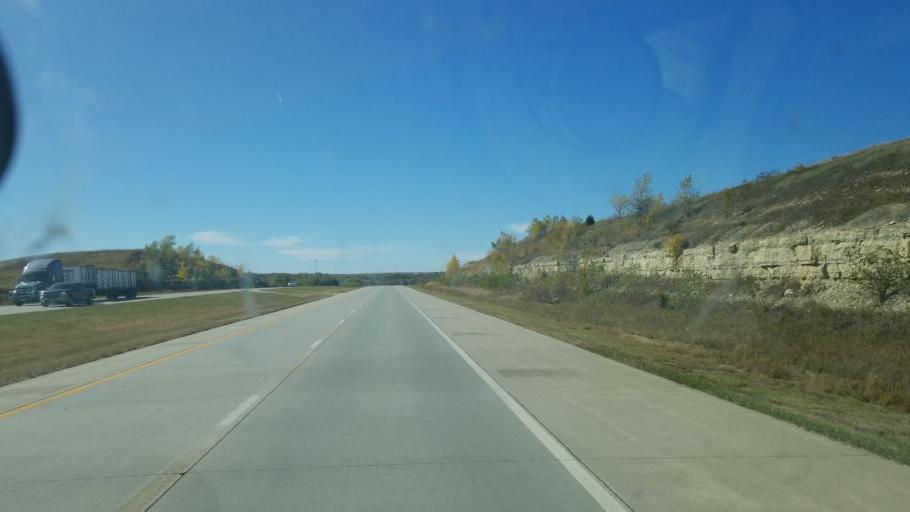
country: US
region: Kansas
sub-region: Riley County
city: Ogden
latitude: 39.0659
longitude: -96.6058
